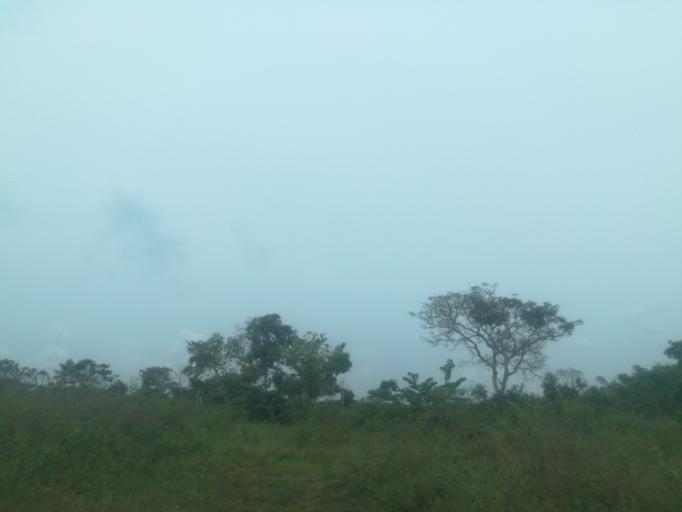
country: NG
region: Ogun
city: Ayetoro
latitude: 7.2696
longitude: 3.1044
